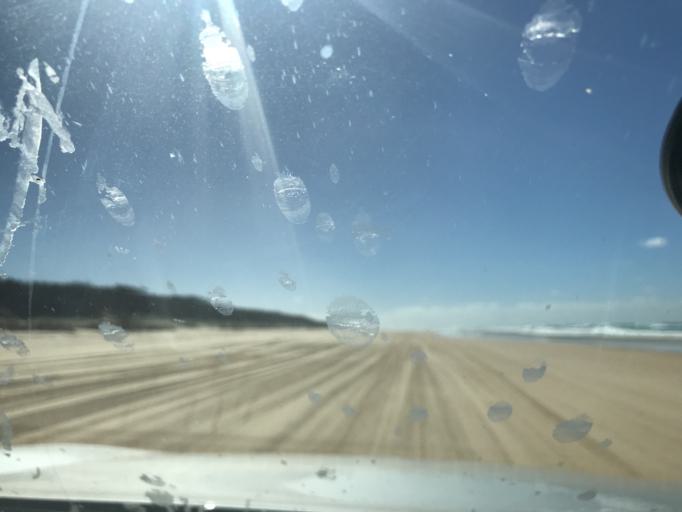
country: AU
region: Queensland
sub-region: Fraser Coast
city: Urangan
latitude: -25.0444
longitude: 153.3438
